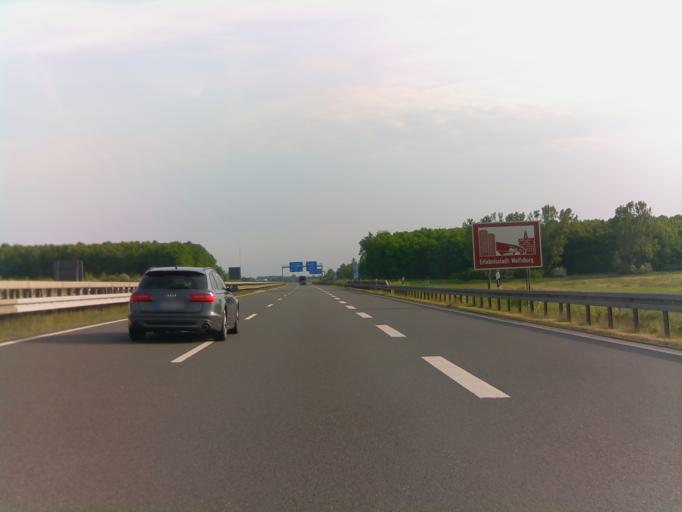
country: DE
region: Lower Saxony
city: Lehre
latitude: 52.2987
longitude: 10.7220
